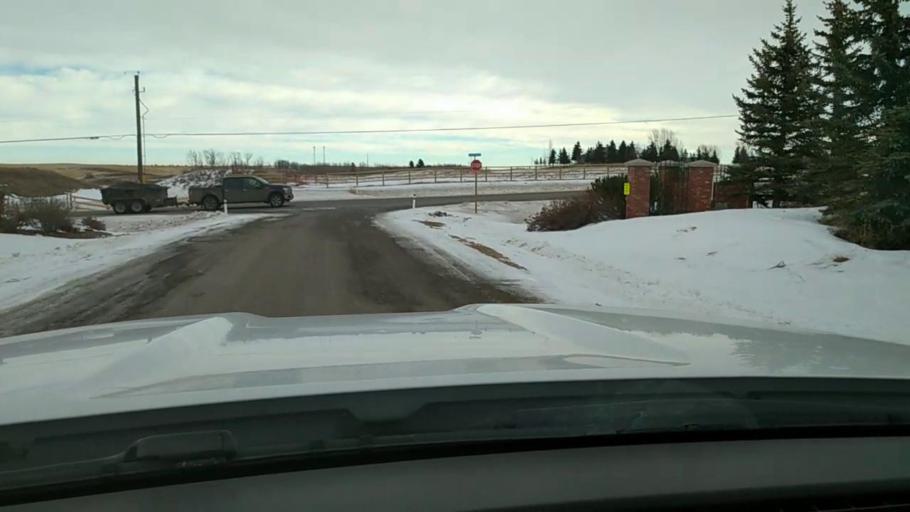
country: CA
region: Alberta
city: Cochrane
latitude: 51.2049
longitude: -114.2814
